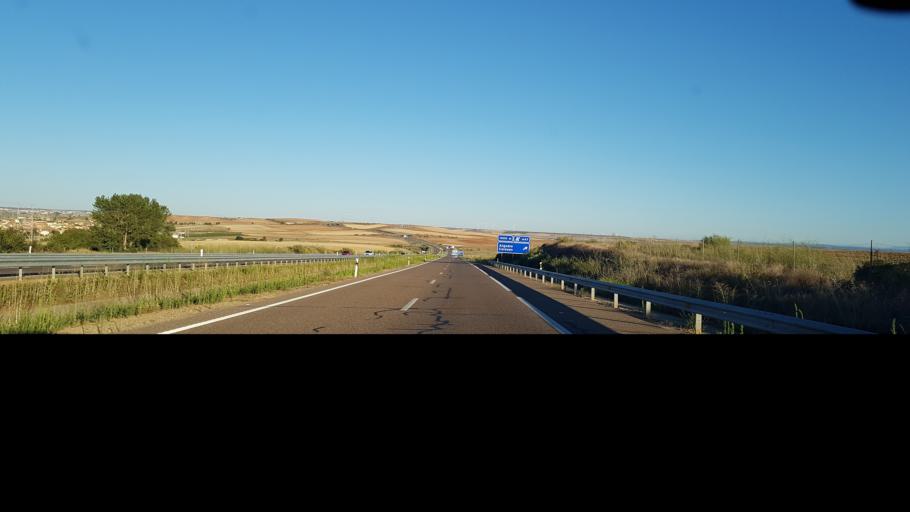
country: ES
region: Castille and Leon
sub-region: Provincia de Zamora
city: Algodre
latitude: 41.5546
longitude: -5.5981
